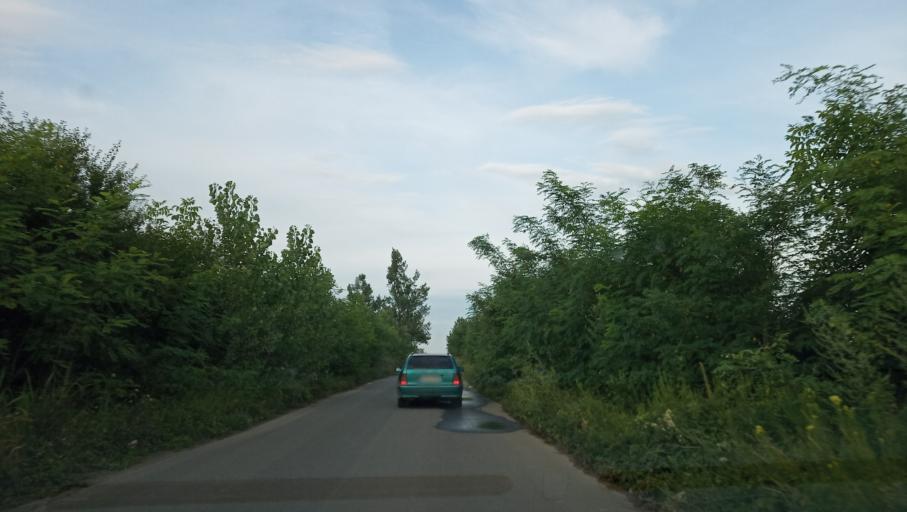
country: RO
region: Giurgiu
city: Gostinari-Vacaresti
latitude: 44.1753
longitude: 26.2071
